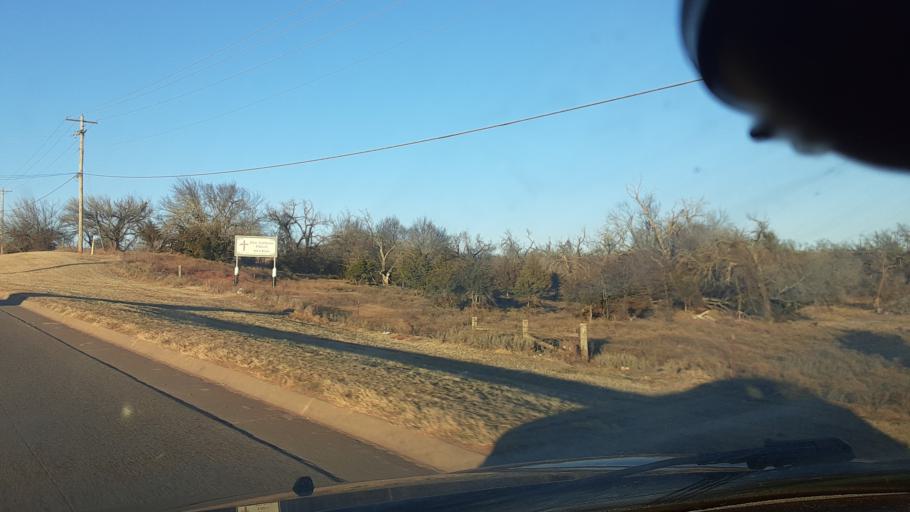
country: US
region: Oklahoma
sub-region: Logan County
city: Guthrie
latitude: 35.8387
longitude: -97.4254
